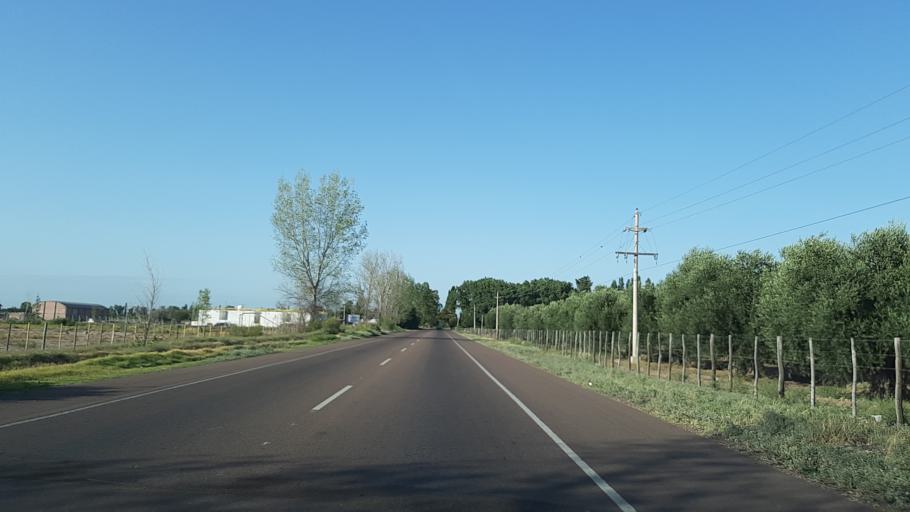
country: AR
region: Mendoza
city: San Martin
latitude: -32.9548
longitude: -68.4332
